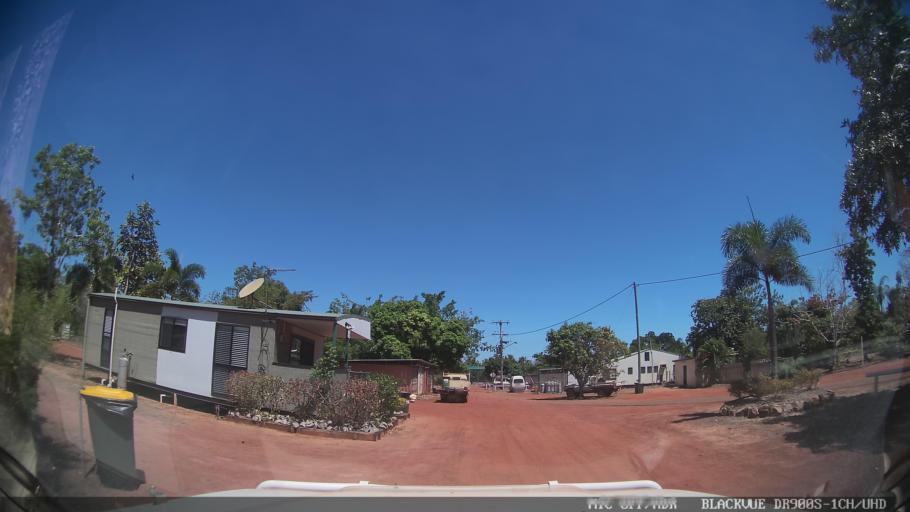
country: AU
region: Queensland
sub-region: Torres
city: Thursday Island
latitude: -10.8468
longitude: 142.3689
